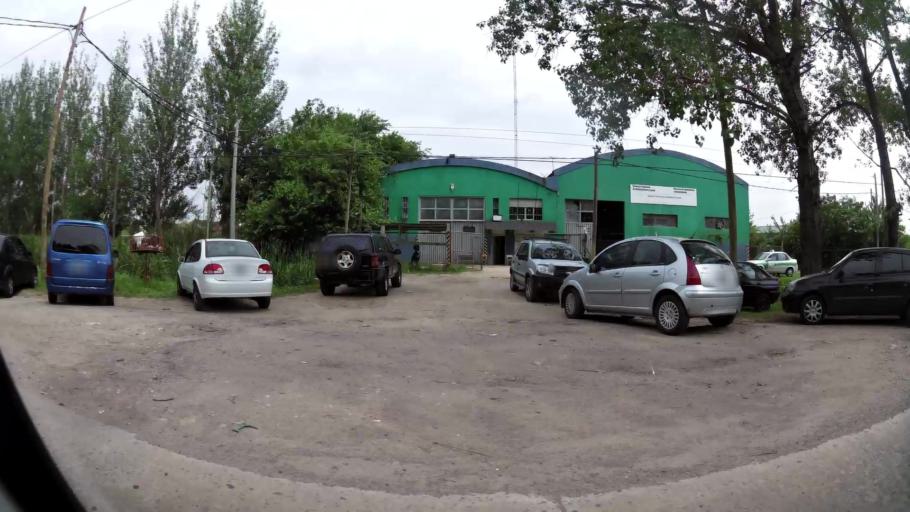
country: AR
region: Buenos Aires
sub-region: Partido de La Plata
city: La Plata
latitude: -34.9114
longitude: -58.0057
